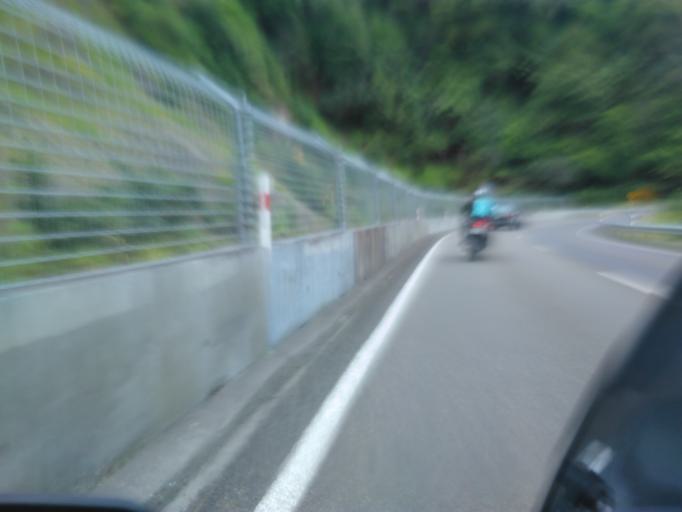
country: NZ
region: Bay of Plenty
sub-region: Opotiki District
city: Opotiki
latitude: -38.3117
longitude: 177.3955
